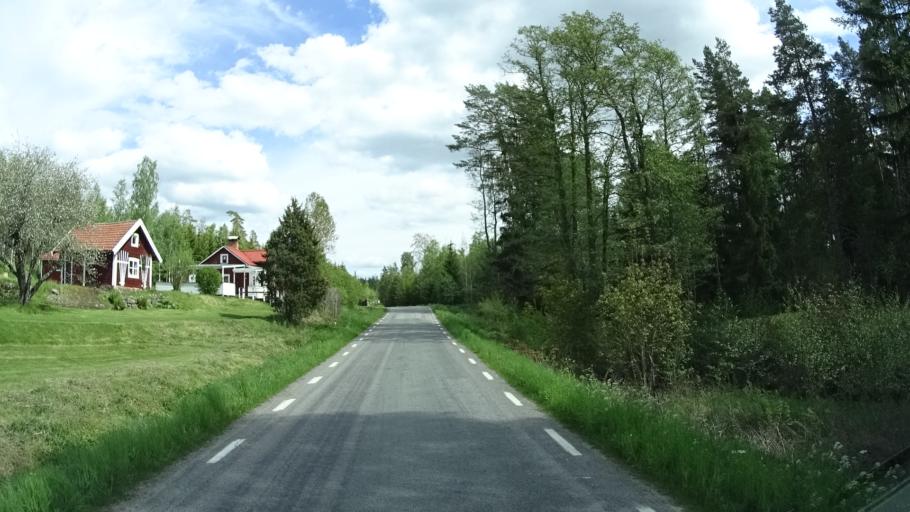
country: SE
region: OEstergoetland
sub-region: Finspangs Kommun
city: Finspang
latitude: 58.6103
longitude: 15.7199
